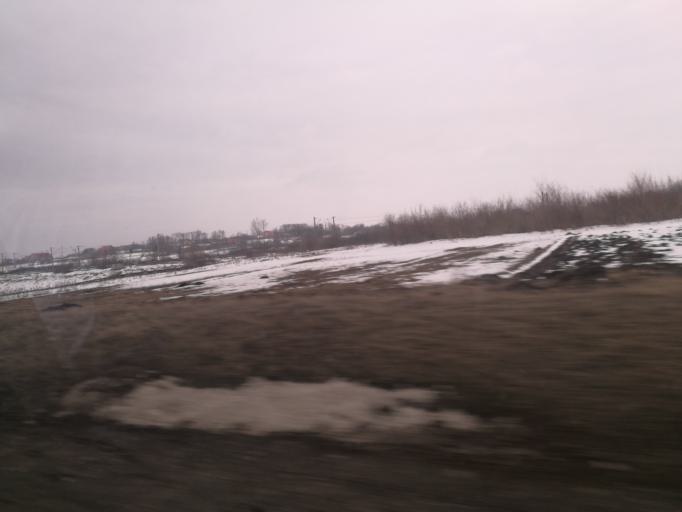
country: RO
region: Iasi
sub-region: Comuna Ruginoasa
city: Rediu
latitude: 47.2454
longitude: 26.8695
